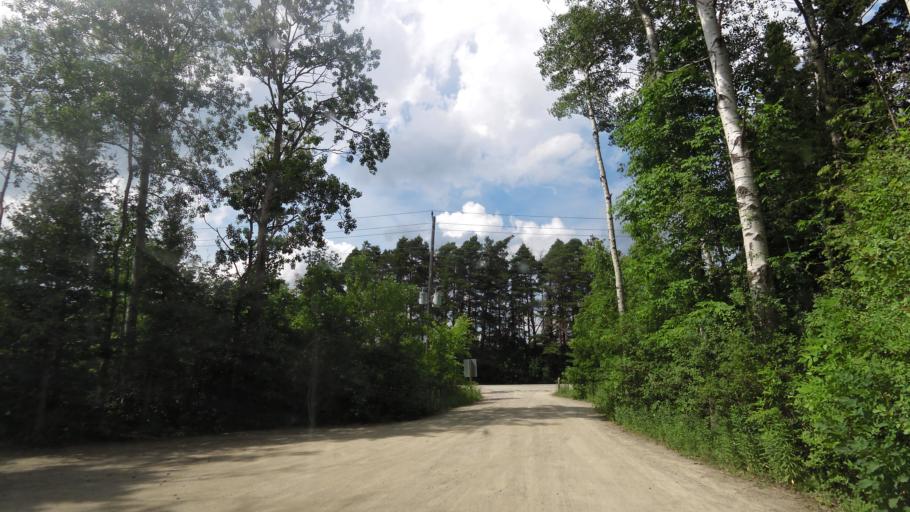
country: CA
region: Ontario
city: Orangeville
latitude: 43.9466
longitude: -80.0997
